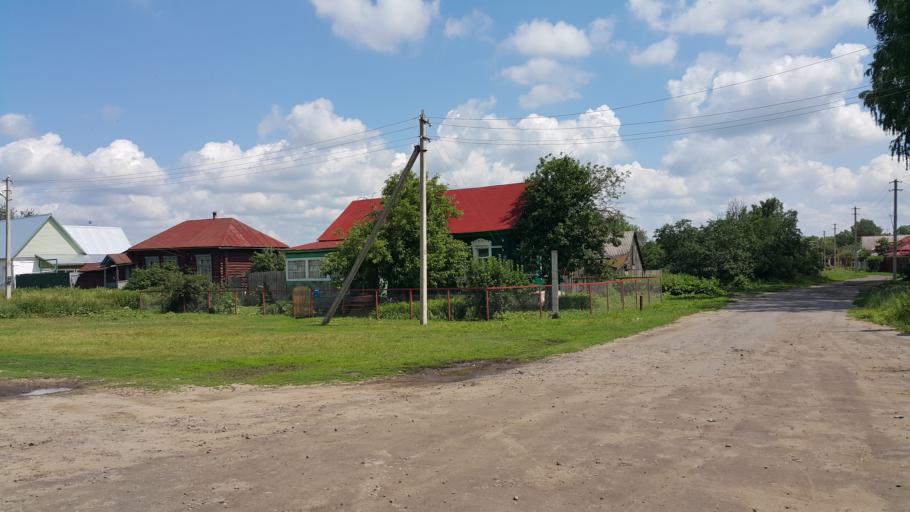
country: RU
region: Tambov
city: Morshansk
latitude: 53.6196
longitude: 41.8509
